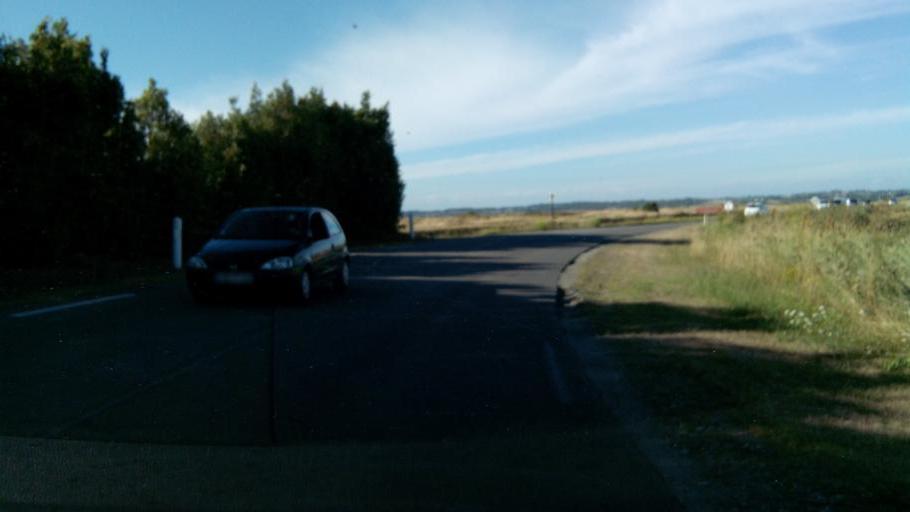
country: FR
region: Pays de la Loire
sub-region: Departement de la Loire-Atlantique
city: Le Pouliguen
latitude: 47.2821
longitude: -2.4526
